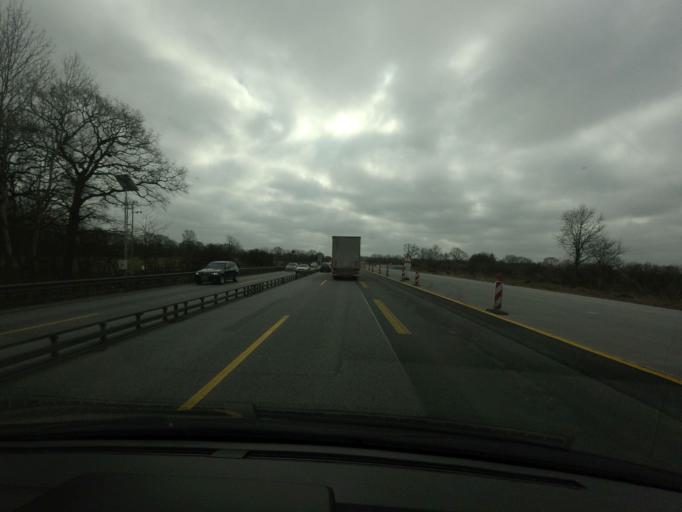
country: DE
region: Schleswig-Holstein
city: Alveslohe
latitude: 53.8073
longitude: 9.9272
